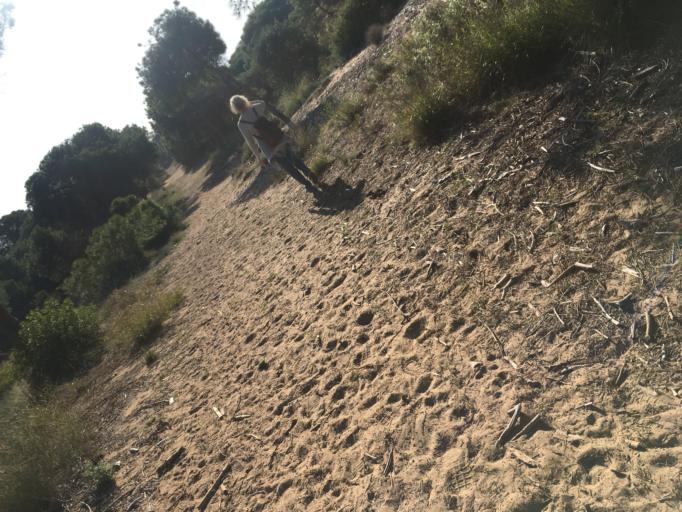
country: ES
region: Valencia
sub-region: Provincia de Alicante
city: Guardamar del Segura
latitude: 38.1323
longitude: -0.6426
